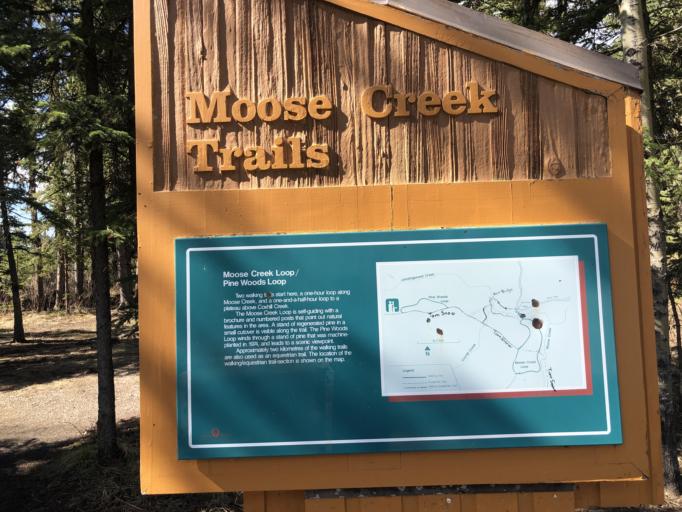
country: CA
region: Alberta
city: Cochrane
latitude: 51.0324
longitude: -114.8094
